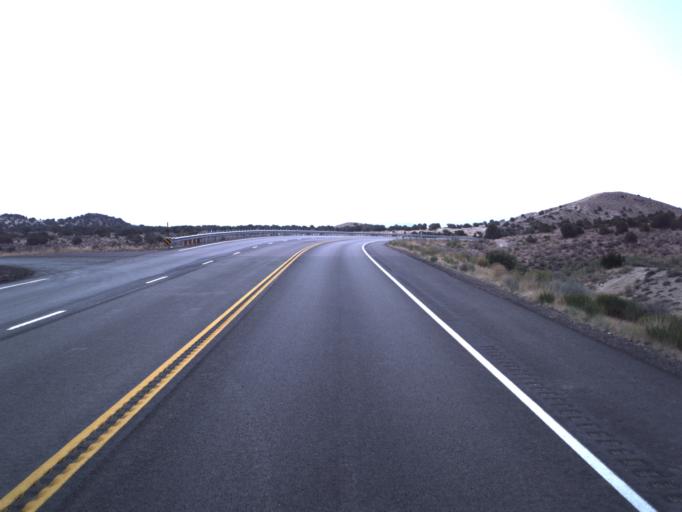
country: US
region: Utah
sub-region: Uintah County
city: Naples
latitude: 40.3445
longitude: -109.4855
